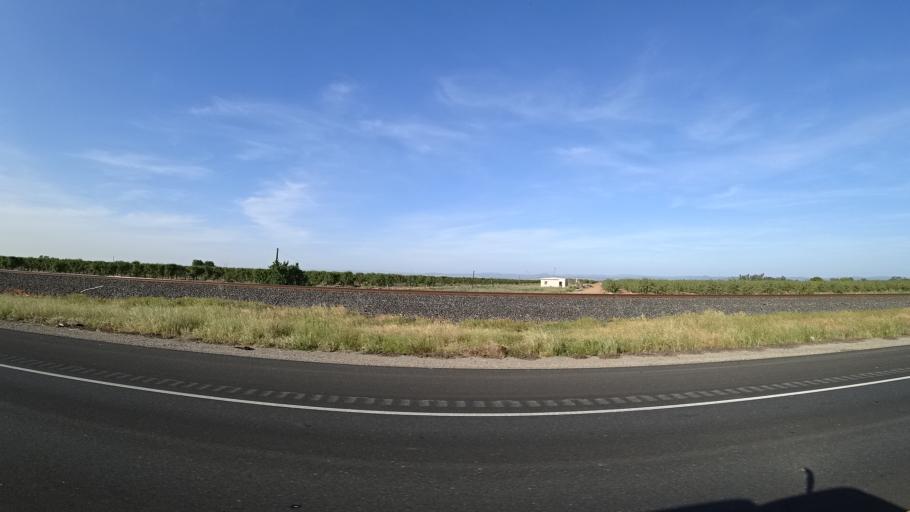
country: US
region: California
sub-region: Yuba County
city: Wheatland
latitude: 39.0276
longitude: -121.4528
